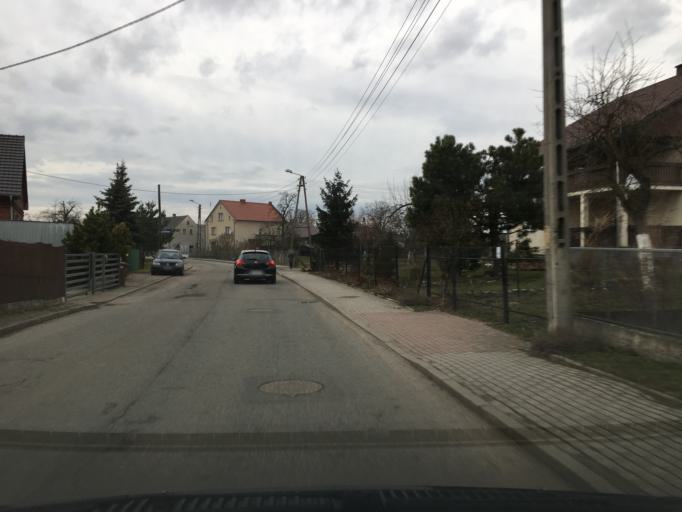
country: PL
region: Opole Voivodeship
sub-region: Powiat kedzierzynsko-kozielski
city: Wiekszyce
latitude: 50.3559
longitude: 18.1227
